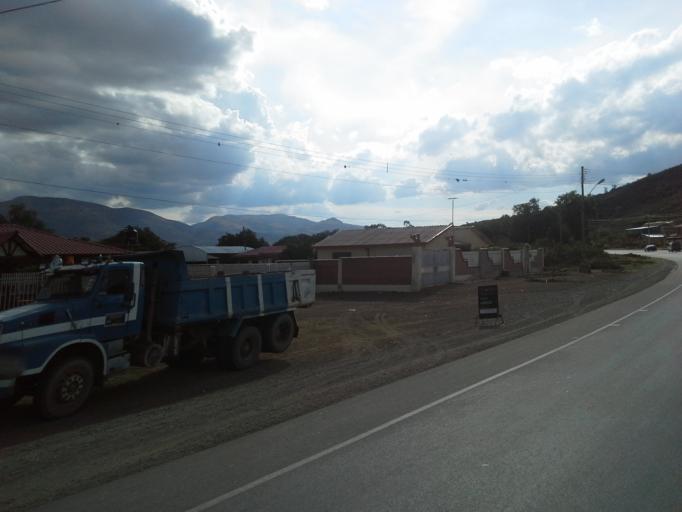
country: BO
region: Cochabamba
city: Tarata
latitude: -17.5414
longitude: -66.0361
